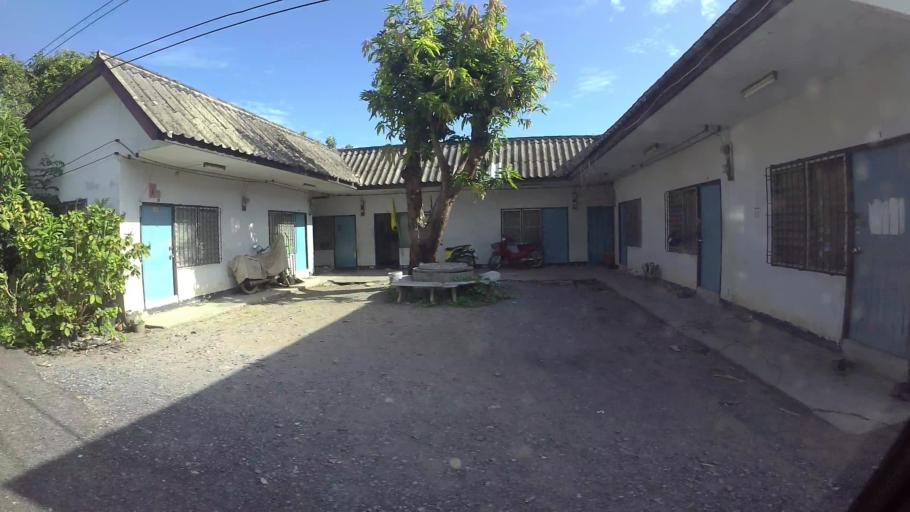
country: TH
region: Chon Buri
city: Sattahip
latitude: 12.6769
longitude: 100.9100
